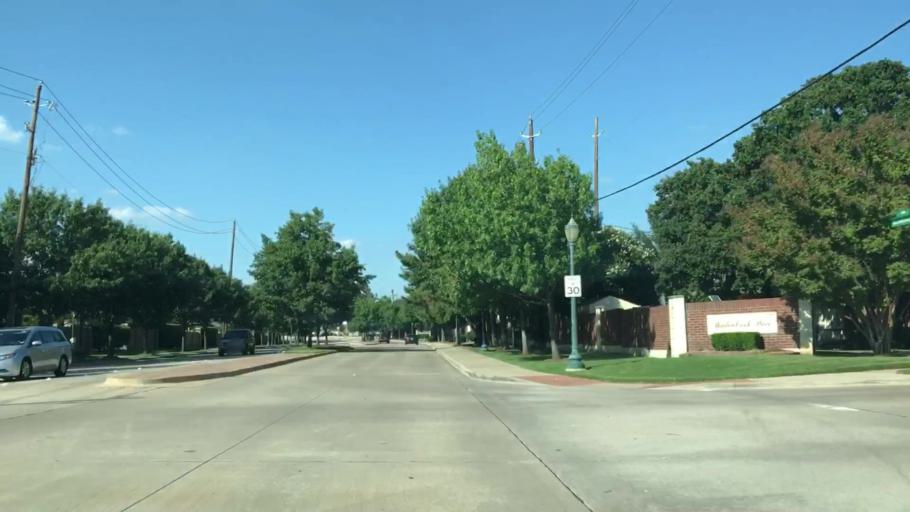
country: US
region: Texas
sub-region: Tarrant County
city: Keller
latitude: 32.9303
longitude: -97.2191
